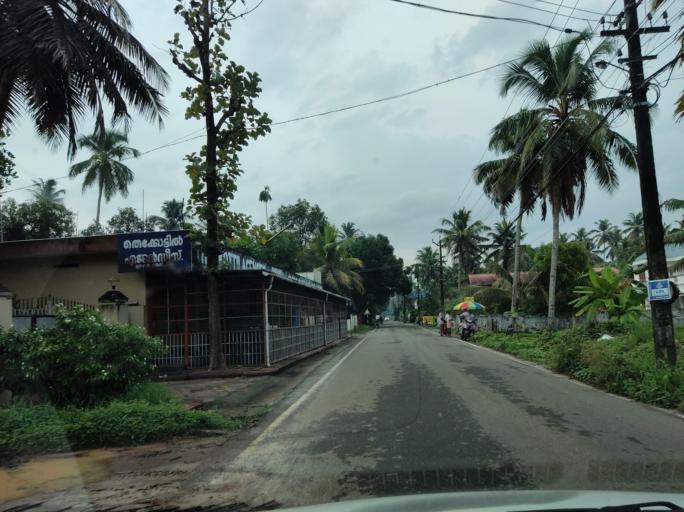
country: IN
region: Kerala
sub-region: Alappuzha
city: Kayankulam
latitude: 9.2107
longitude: 76.4616
